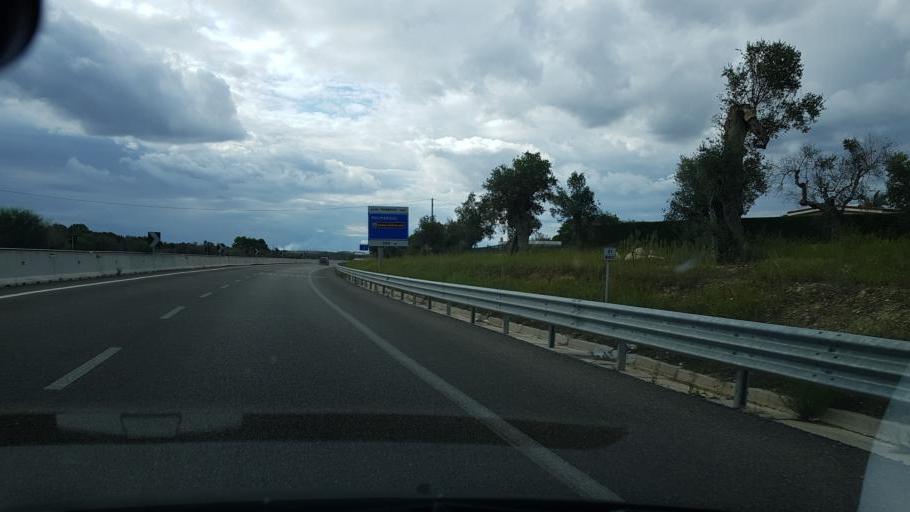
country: IT
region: Apulia
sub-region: Provincia di Lecce
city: Palmariggi
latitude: 40.1262
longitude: 18.3779
